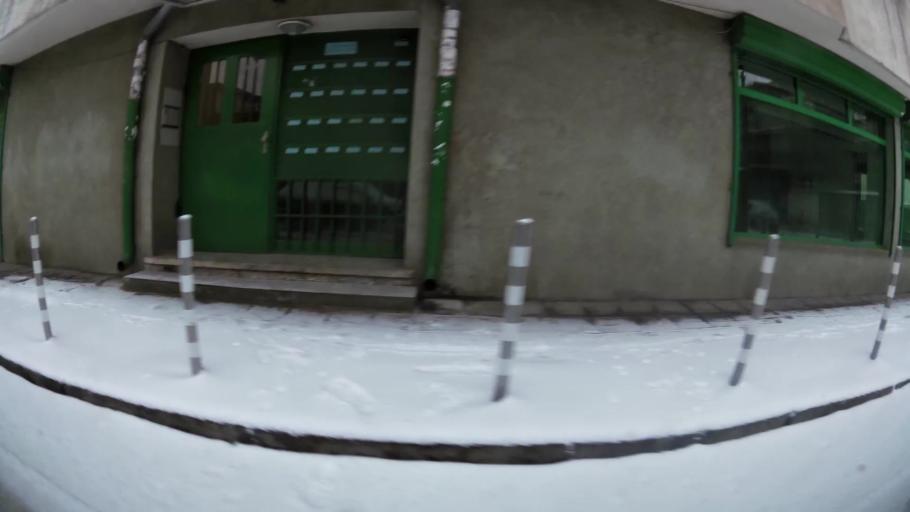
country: BG
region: Sofia-Capital
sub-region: Stolichna Obshtina
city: Sofia
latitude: 42.7054
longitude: 23.3079
